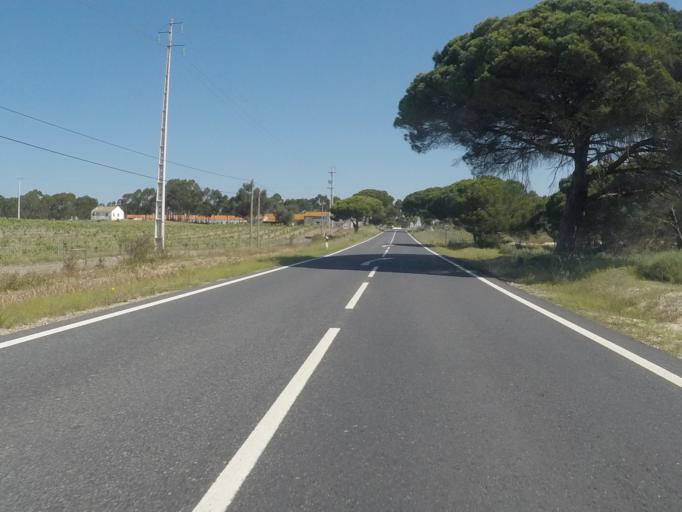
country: PT
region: Setubal
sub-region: Grandola
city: Grandola
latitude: 38.2531
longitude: -8.7375
